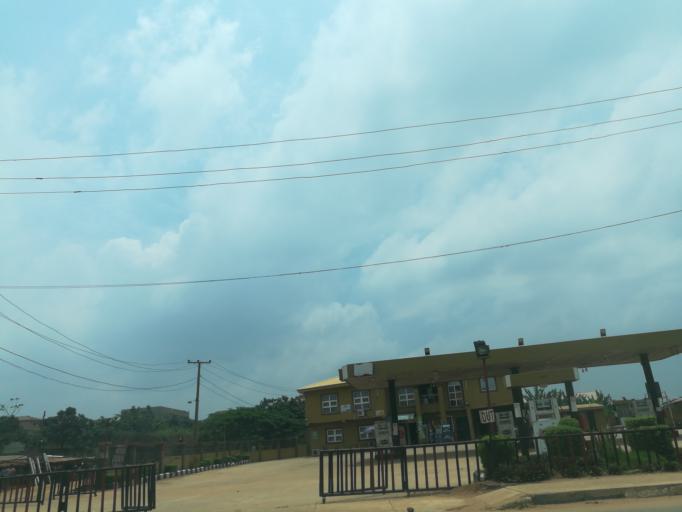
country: NG
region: Lagos
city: Ikorodu
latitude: 6.6249
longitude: 3.5263
